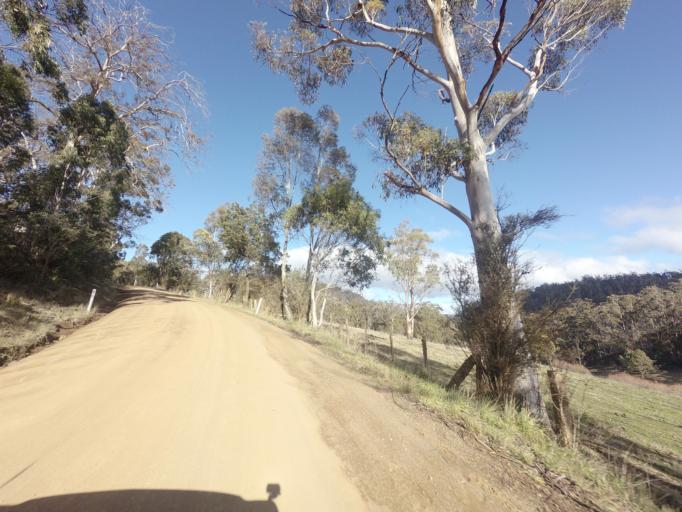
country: AU
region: Tasmania
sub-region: Derwent Valley
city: New Norfolk
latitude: -42.7087
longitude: 147.0222
